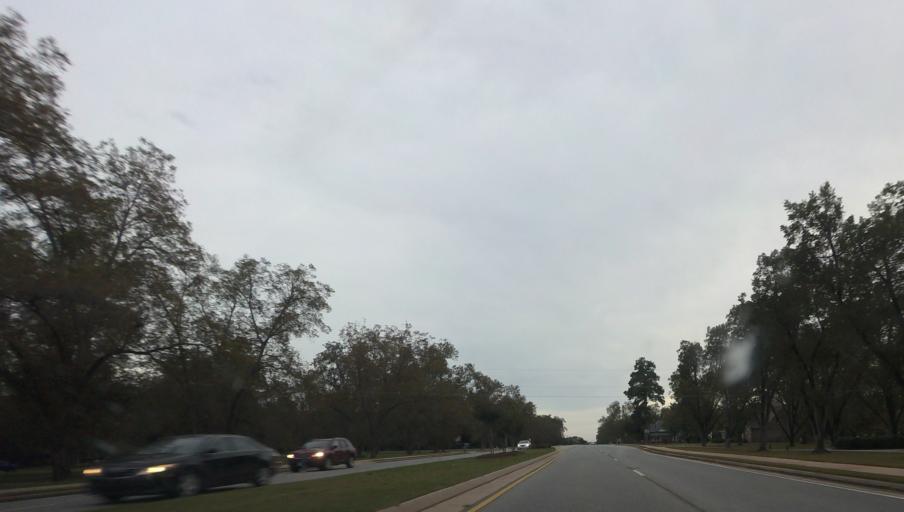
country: US
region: Georgia
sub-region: Houston County
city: Perry
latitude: 32.5264
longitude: -83.6624
